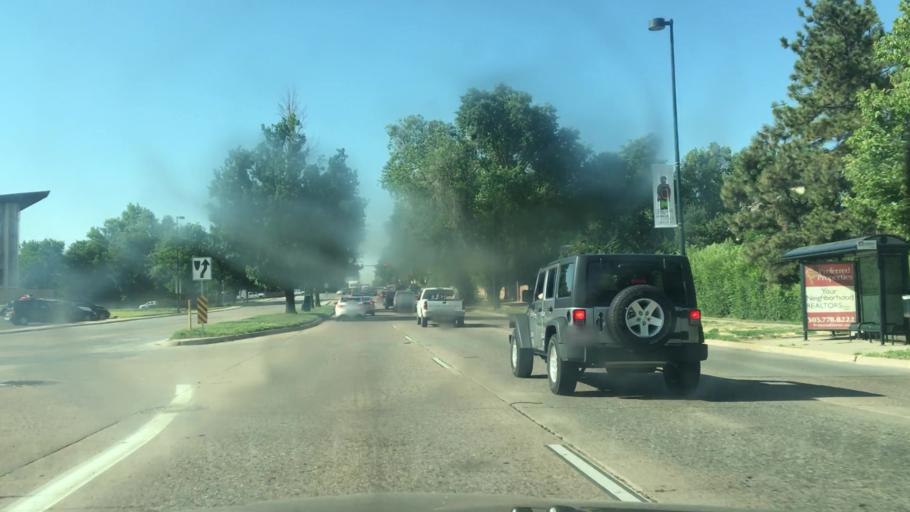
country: US
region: Colorado
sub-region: Arapahoe County
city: Glendale
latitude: 39.7131
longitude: -104.9593
